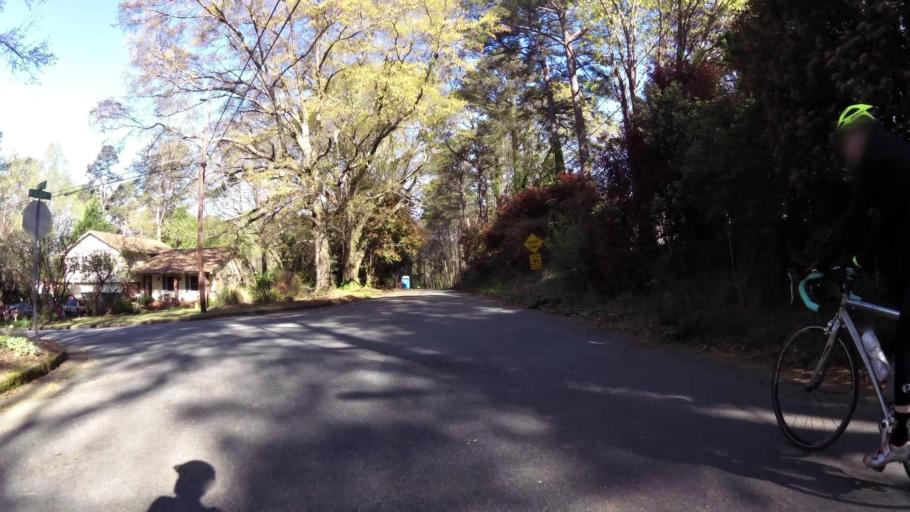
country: US
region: Georgia
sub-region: DeKalb County
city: Clarkston
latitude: 33.8316
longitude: -84.2608
